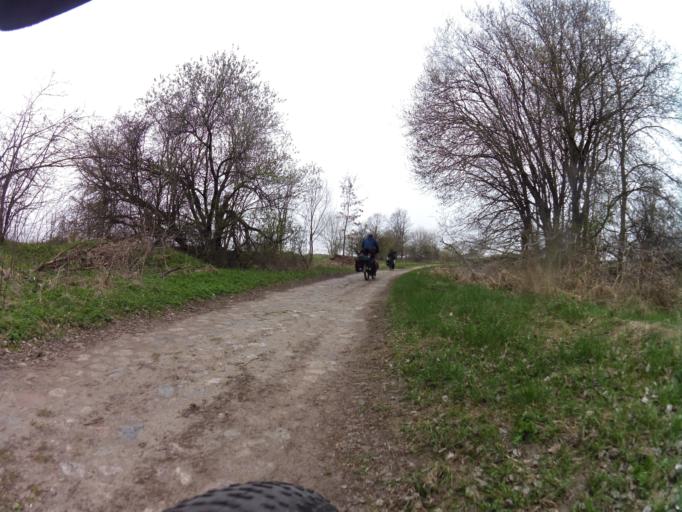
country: PL
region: West Pomeranian Voivodeship
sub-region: Powiat koszalinski
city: Bobolice
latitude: 53.9949
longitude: 16.6812
